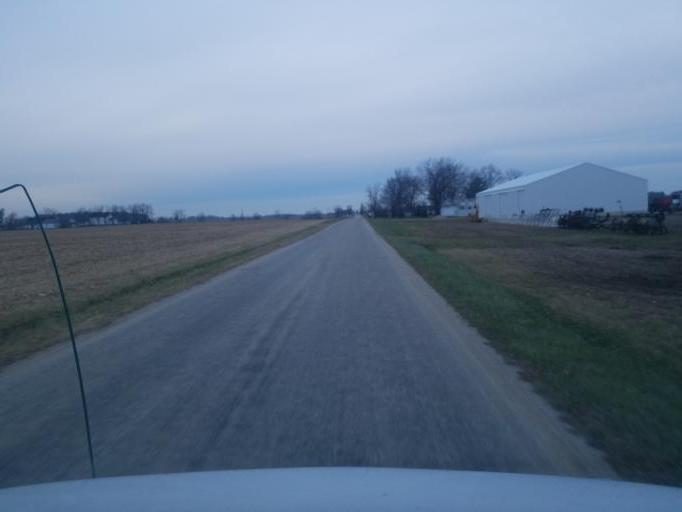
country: US
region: Indiana
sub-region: Adams County
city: Decatur
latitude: 40.7420
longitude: -84.8796
